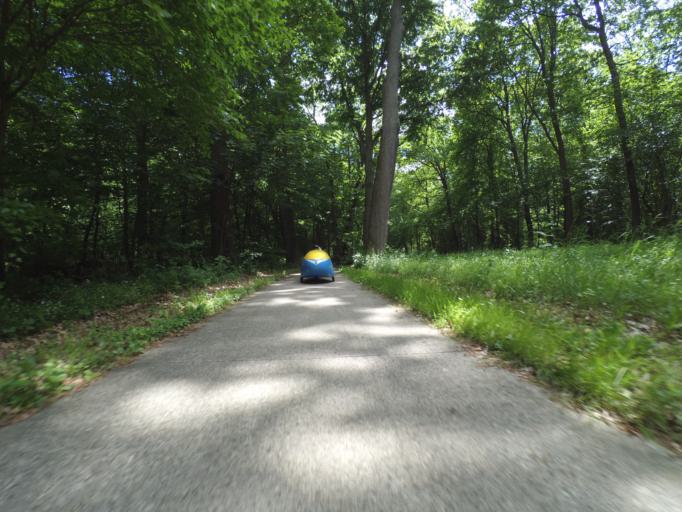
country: DE
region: Lower Saxony
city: Edemissen
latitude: 52.4008
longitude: 10.2422
